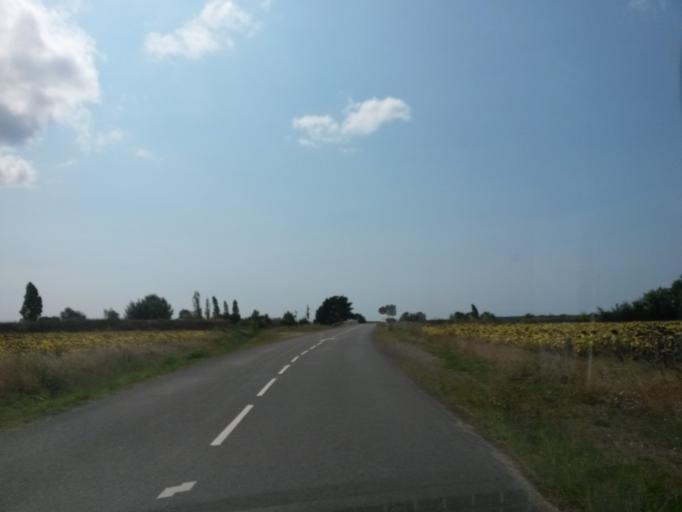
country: FR
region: Pays de la Loire
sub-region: Departement de la Vendee
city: Saint-Hilaire-de-Talmont
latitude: 46.4595
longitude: -1.6179
